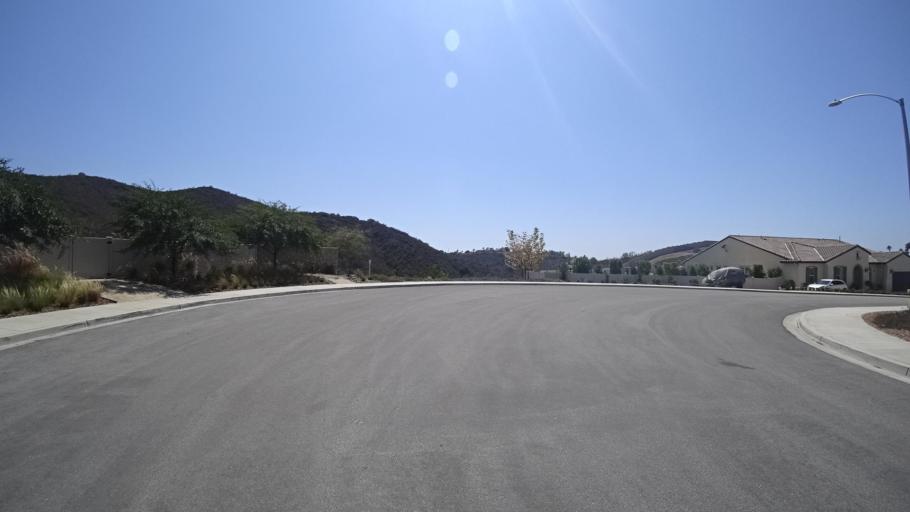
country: US
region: California
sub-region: San Diego County
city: San Marcos
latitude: 33.1802
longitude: -117.1937
